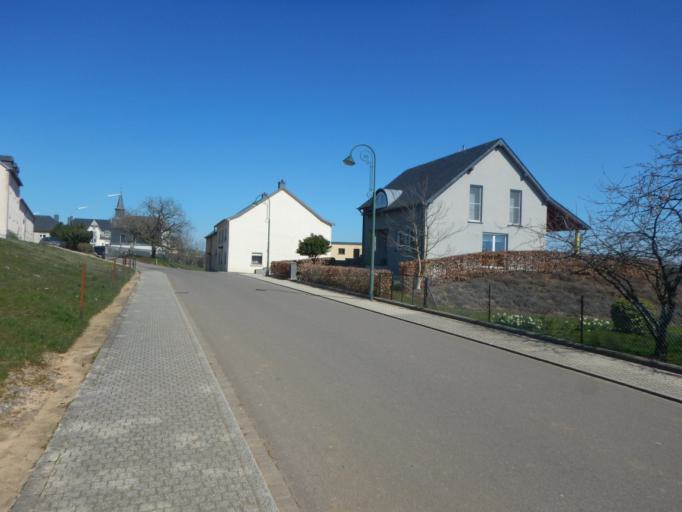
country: LU
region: Luxembourg
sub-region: Canton de Capellen
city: Garnich
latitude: 49.6004
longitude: 5.9466
